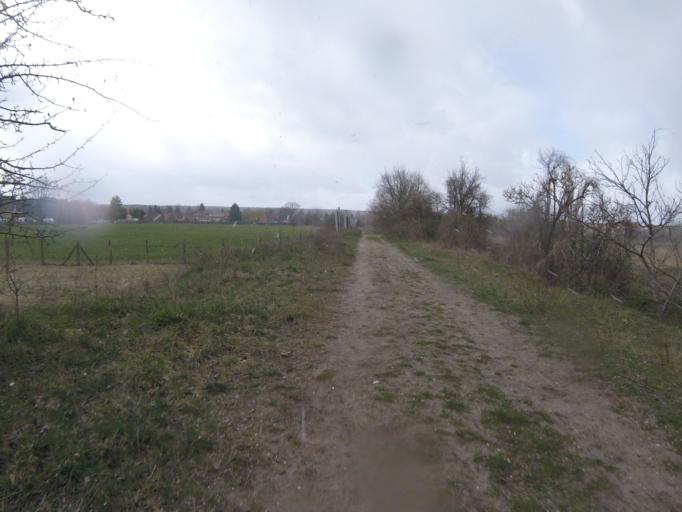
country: DE
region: Brandenburg
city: Schwerin
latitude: 52.2012
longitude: 13.5904
